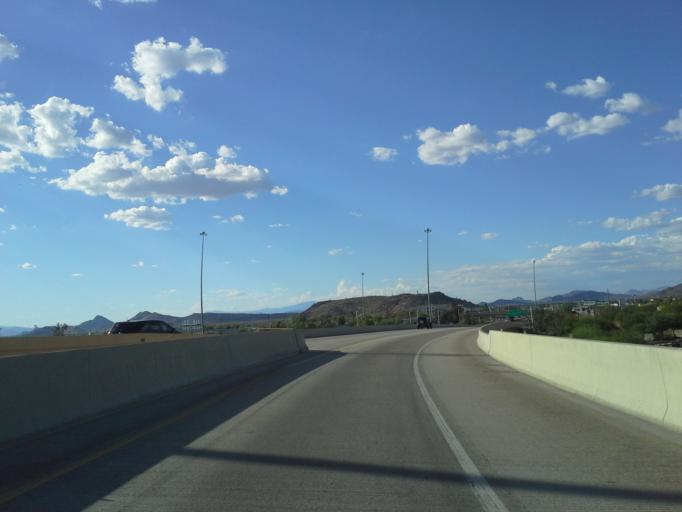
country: US
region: Arizona
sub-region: Maricopa County
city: Glendale
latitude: 33.6709
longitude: -112.1124
